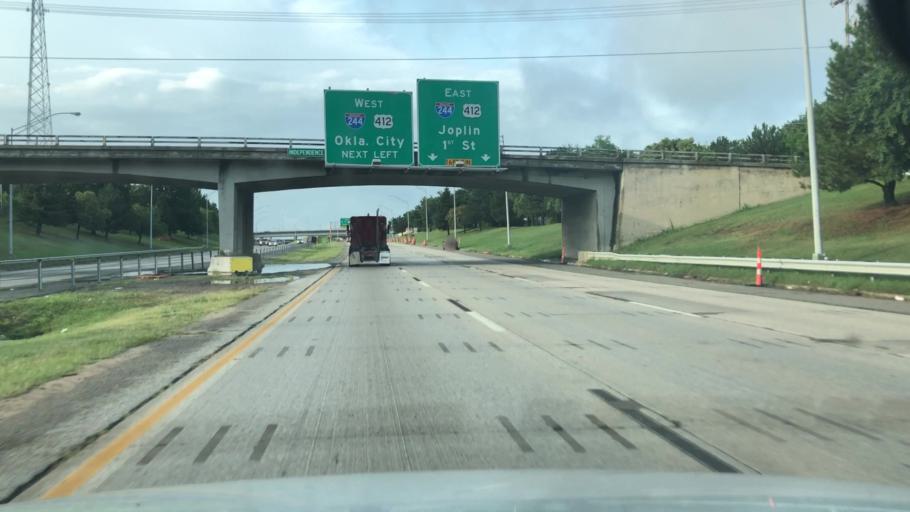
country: US
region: Oklahoma
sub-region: Tulsa County
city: Tulsa
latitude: 36.1665
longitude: -95.9806
